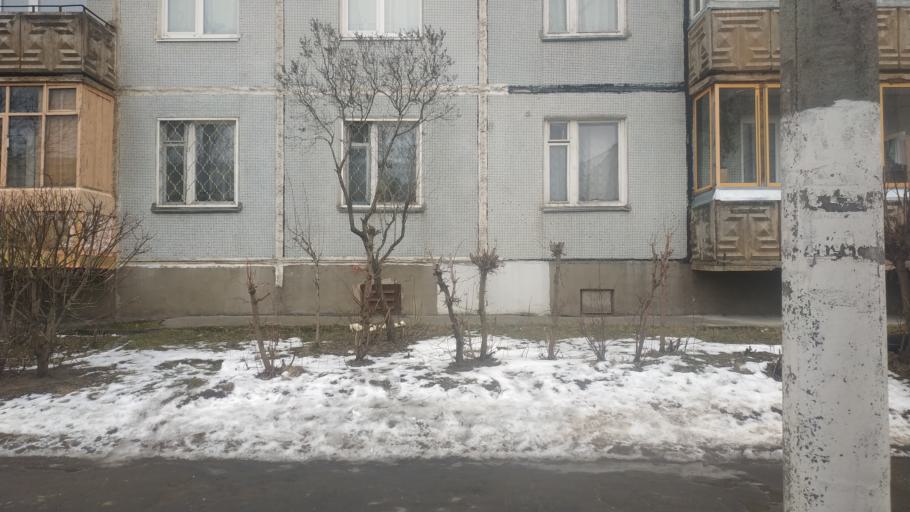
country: RU
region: Tverskaya
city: Tver
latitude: 56.8722
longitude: 35.8890
